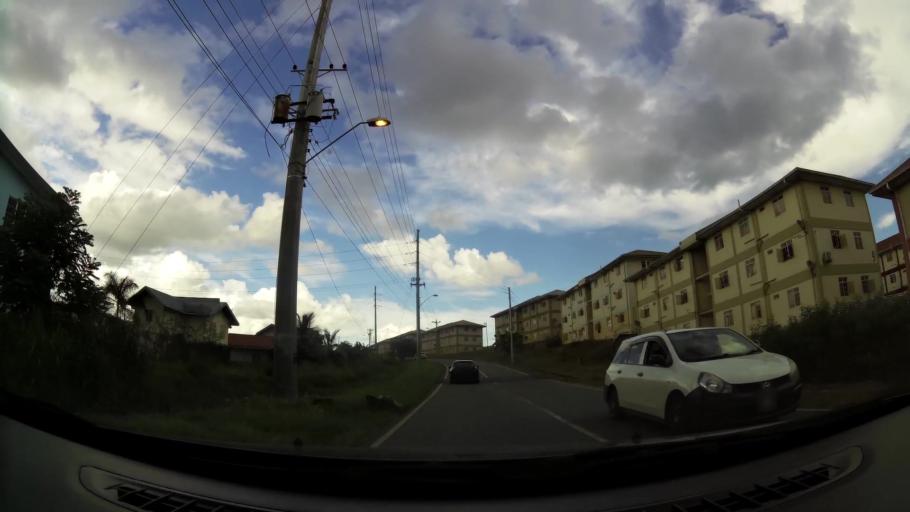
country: TT
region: City of San Fernando
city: Mon Repos
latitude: 10.2653
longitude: -61.4444
